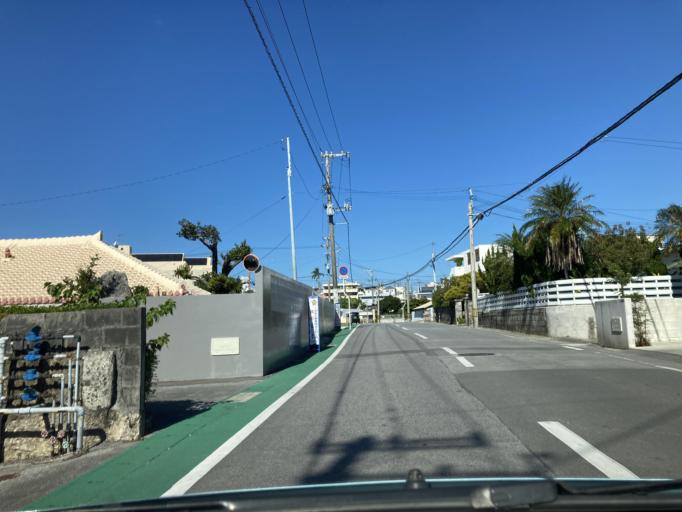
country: JP
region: Okinawa
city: Okinawa
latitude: 26.3557
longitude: 127.8247
